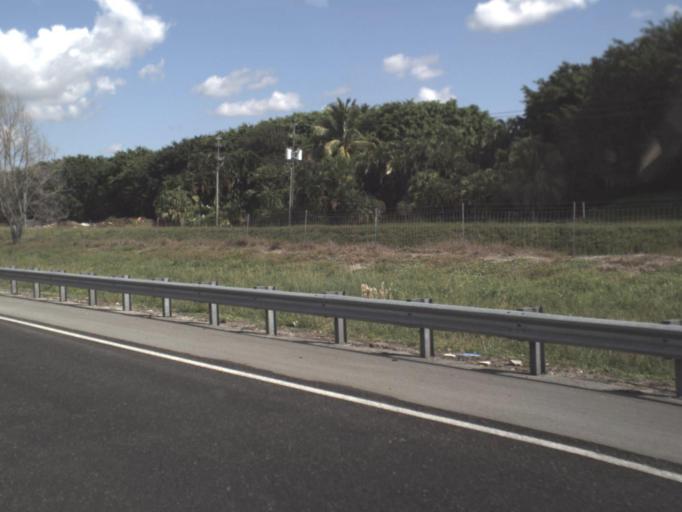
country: US
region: Florida
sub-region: Palm Beach County
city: Boca Del Mar
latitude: 26.3787
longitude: -80.1708
